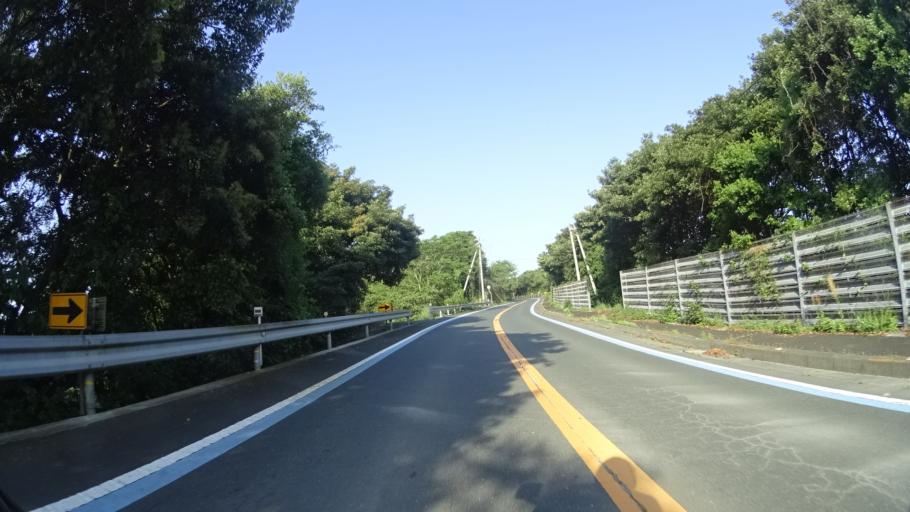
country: JP
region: Ehime
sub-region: Nishiuwa-gun
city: Ikata-cho
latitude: 33.4766
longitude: 132.2966
